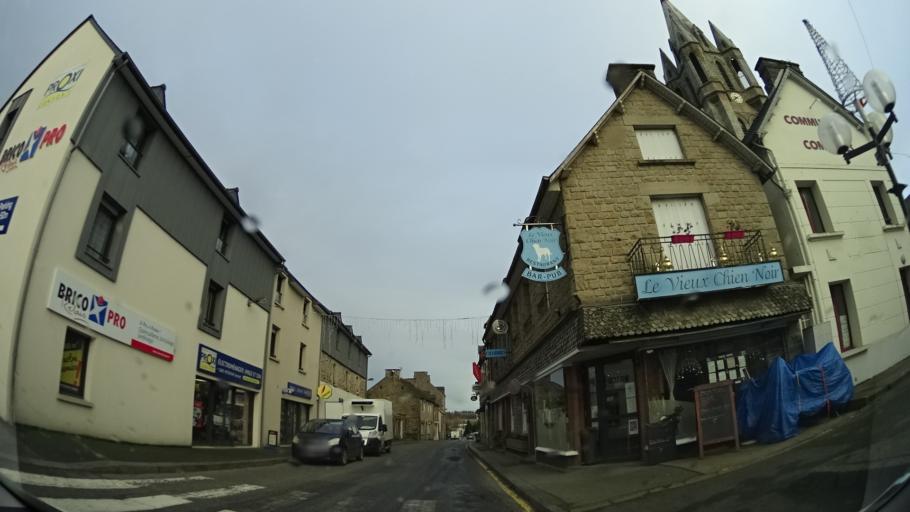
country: FR
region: Brittany
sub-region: Departement des Cotes-d'Armor
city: Evran
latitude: 48.3822
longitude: -1.9805
